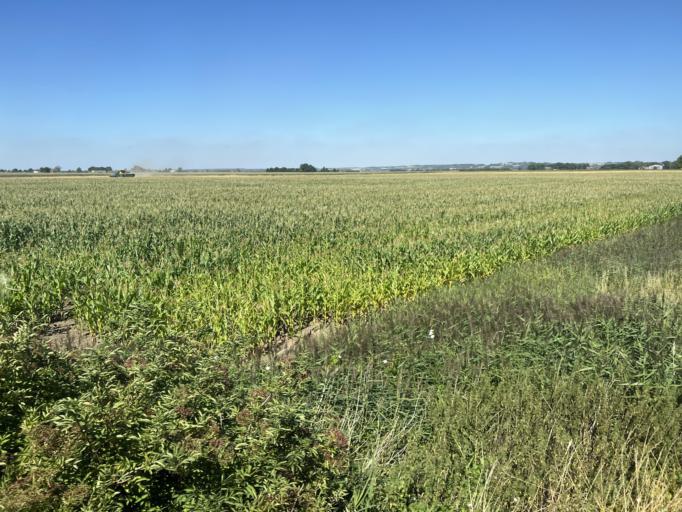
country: GB
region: England
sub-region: Lincolnshire
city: Spilsby
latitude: 53.1016
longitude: 0.1121
